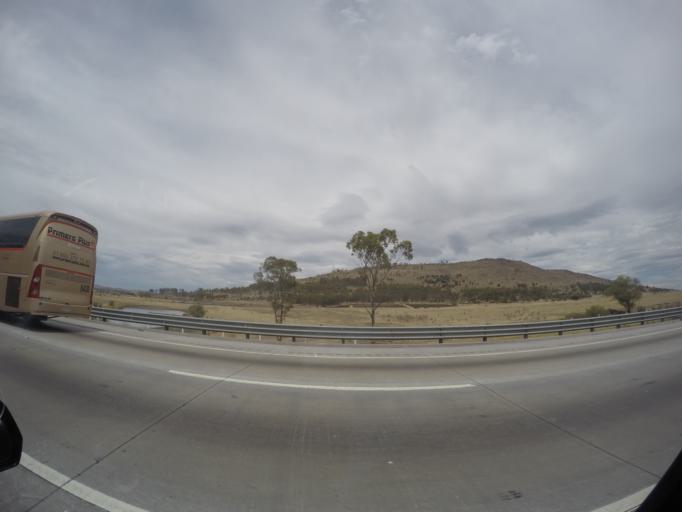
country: MX
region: Mexico
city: San Francisco Soyaniquilpan
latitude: 20.0079
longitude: -99.5054
